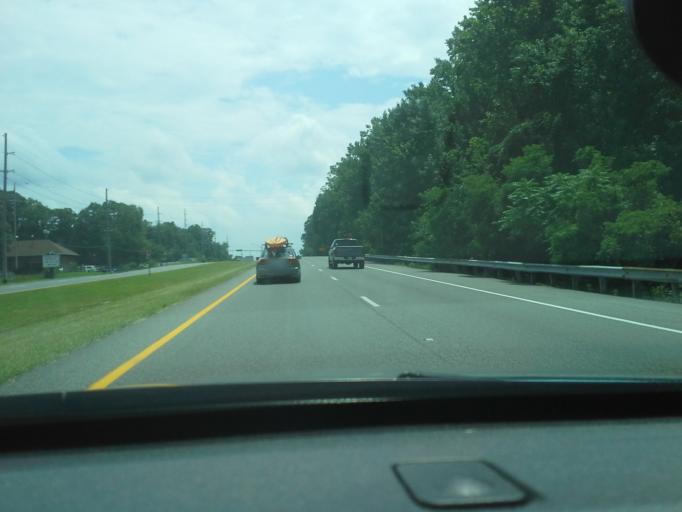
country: US
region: Maryland
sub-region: Calvert County
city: Dunkirk Town Center
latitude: 38.6830
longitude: -76.6339
